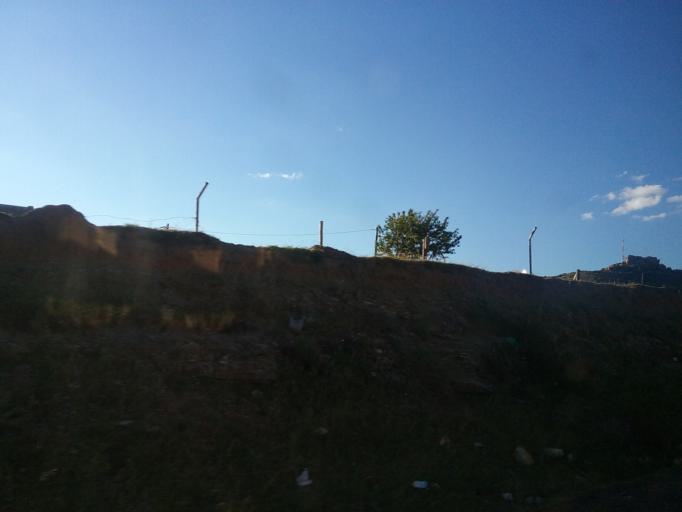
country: LS
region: Mohale's Hoek District
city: Mohale's Hoek
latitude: -30.1520
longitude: 27.4421
